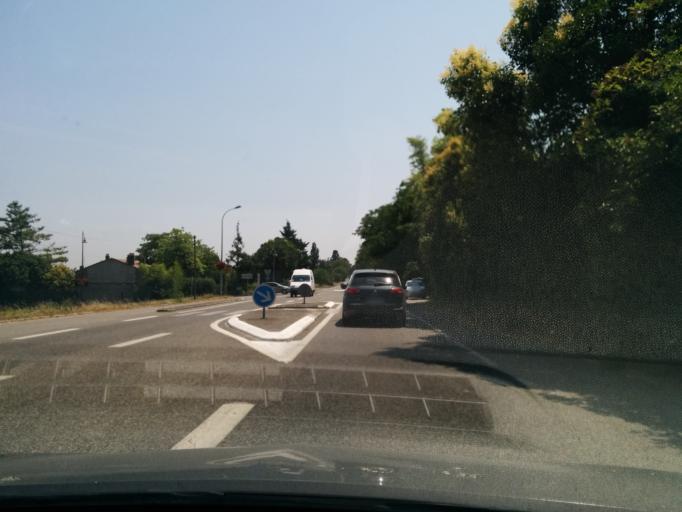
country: FR
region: Midi-Pyrenees
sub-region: Departement de la Haute-Garonne
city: Pechabou
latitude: 43.5035
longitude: 1.5105
